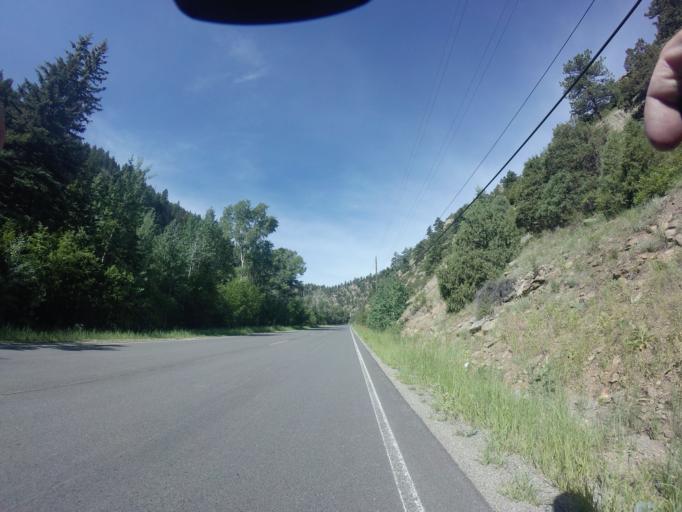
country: US
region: Colorado
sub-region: Clear Creek County
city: Idaho Springs
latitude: 39.7225
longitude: -105.5649
